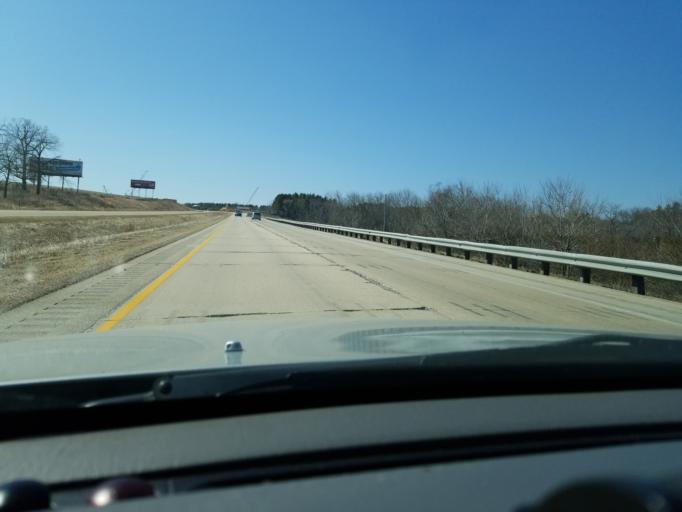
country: US
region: Wisconsin
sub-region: Iowa County
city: Barneveld
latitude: 42.9954
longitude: -89.9914
